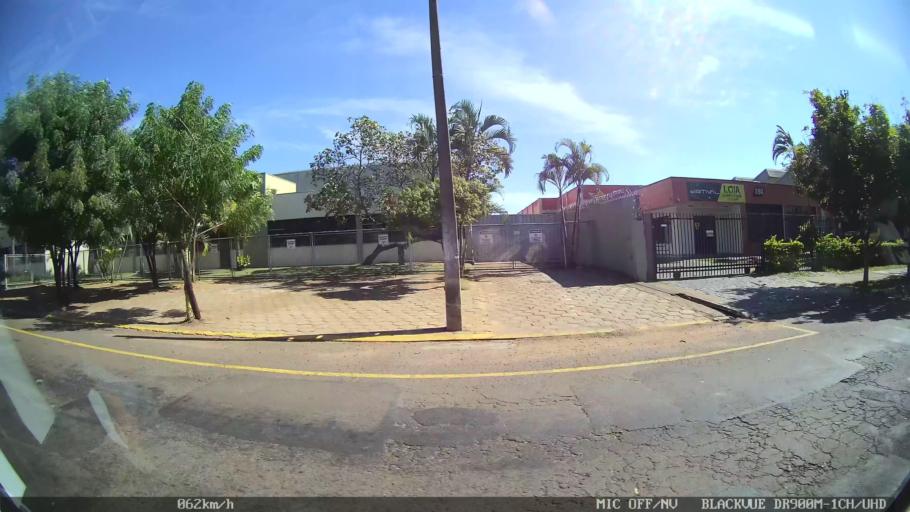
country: BR
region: Sao Paulo
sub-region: Franca
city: Franca
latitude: -20.5505
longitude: -47.4371
